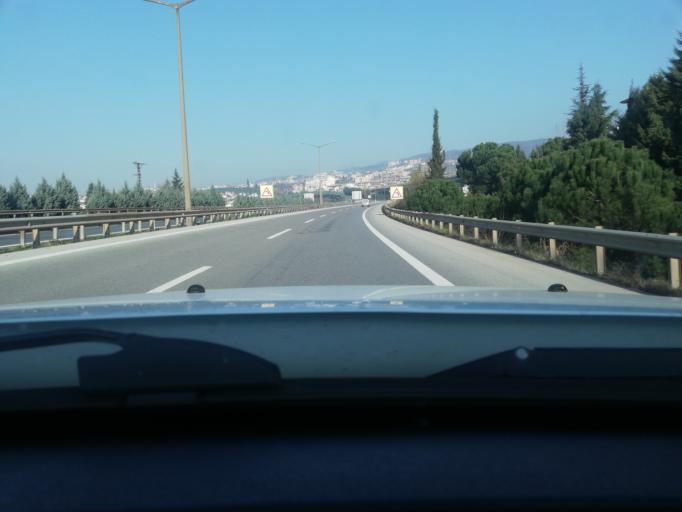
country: TR
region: Kocaeli
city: Derince
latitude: 40.7640
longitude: 29.8560
